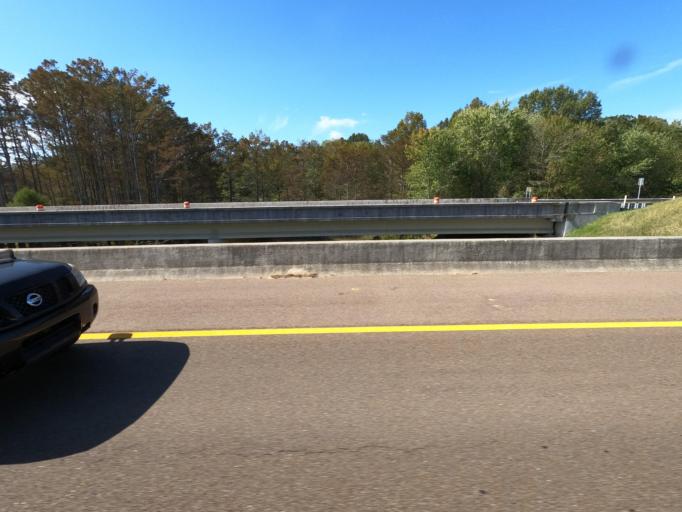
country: US
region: Tennessee
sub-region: Dyer County
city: Dyersburg
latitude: 35.9984
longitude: -89.3418
